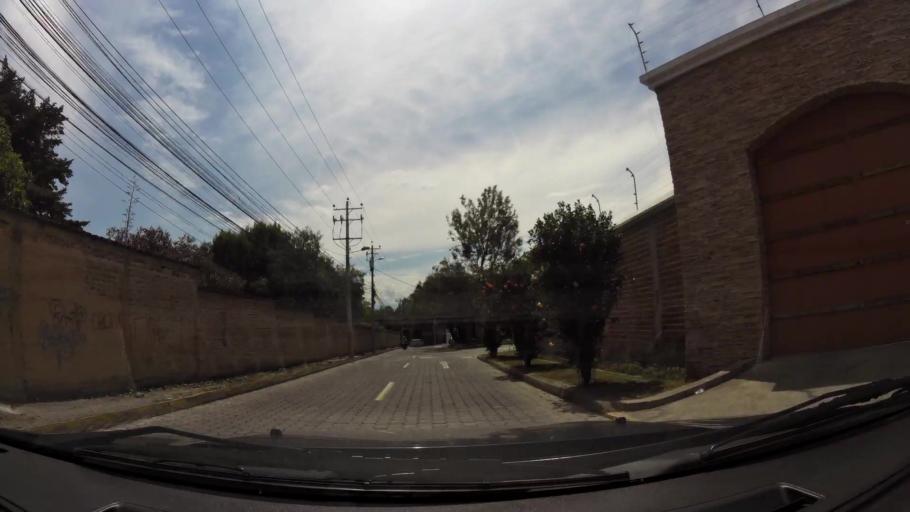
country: EC
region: Pichincha
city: Quito
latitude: -0.2097
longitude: -78.4133
